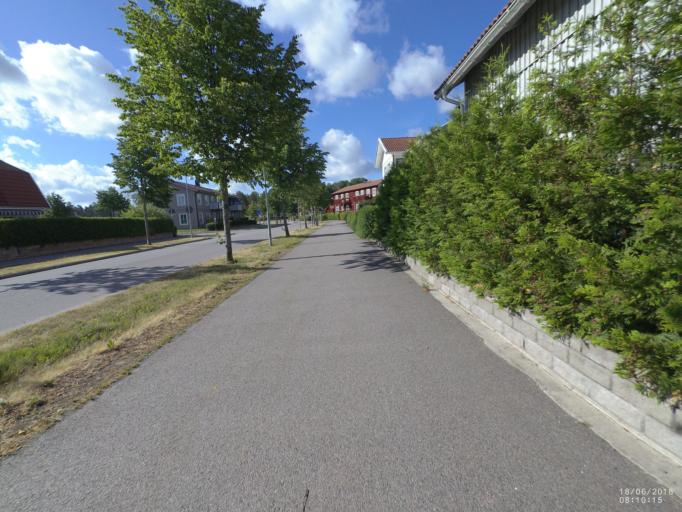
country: SE
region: Soedermanland
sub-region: Nykopings Kommun
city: Nykoping
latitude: 58.7355
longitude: 17.0212
